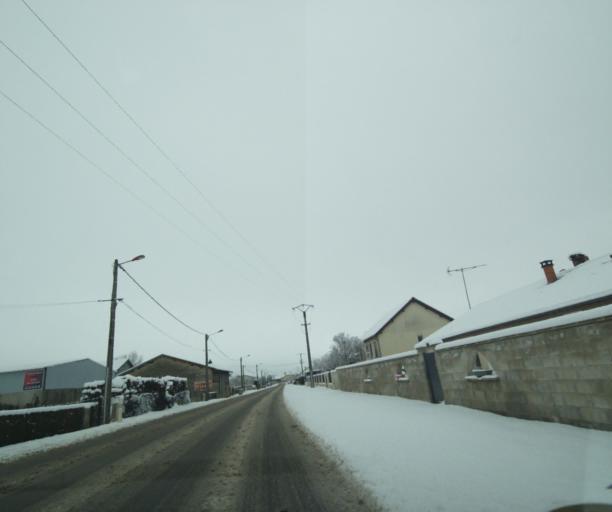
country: FR
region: Champagne-Ardenne
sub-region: Departement de la Haute-Marne
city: Wassy
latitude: 48.5302
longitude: 4.9273
